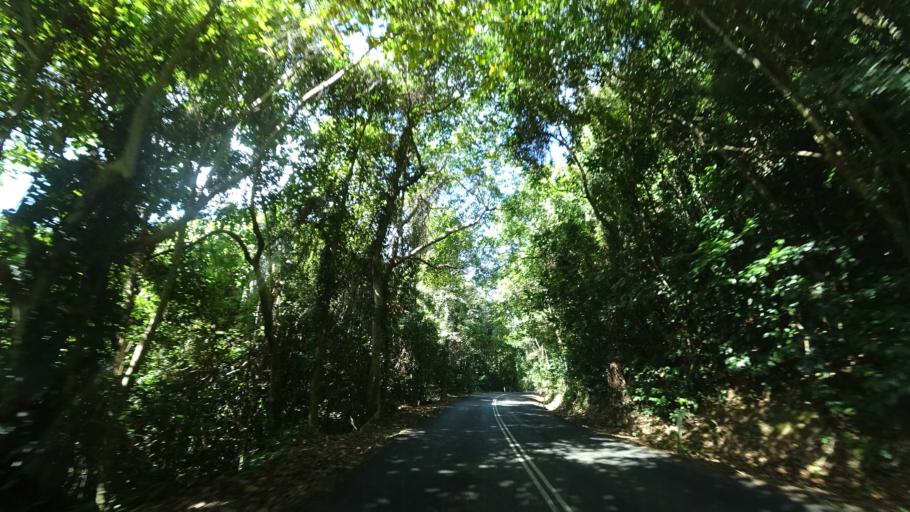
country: AU
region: Queensland
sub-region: Cairns
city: Port Douglas
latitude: -16.1182
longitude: 145.4569
